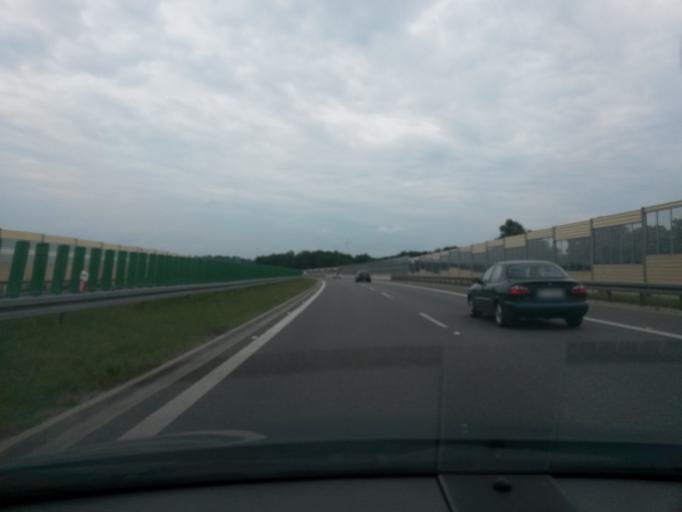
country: PL
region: Masovian Voivodeship
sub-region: Powiat zyrardowski
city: Radziejowice
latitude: 52.0025
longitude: 20.5613
